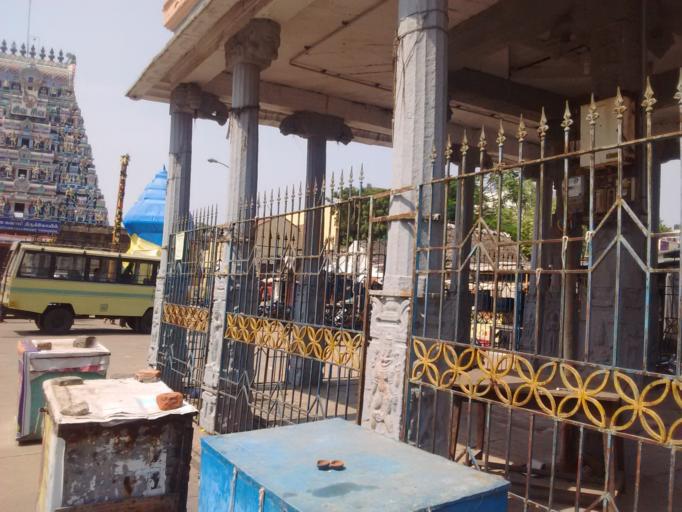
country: IN
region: Tamil Nadu
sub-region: Thiruvallur
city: Tiruvottiyur
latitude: 13.1608
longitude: 80.3002
